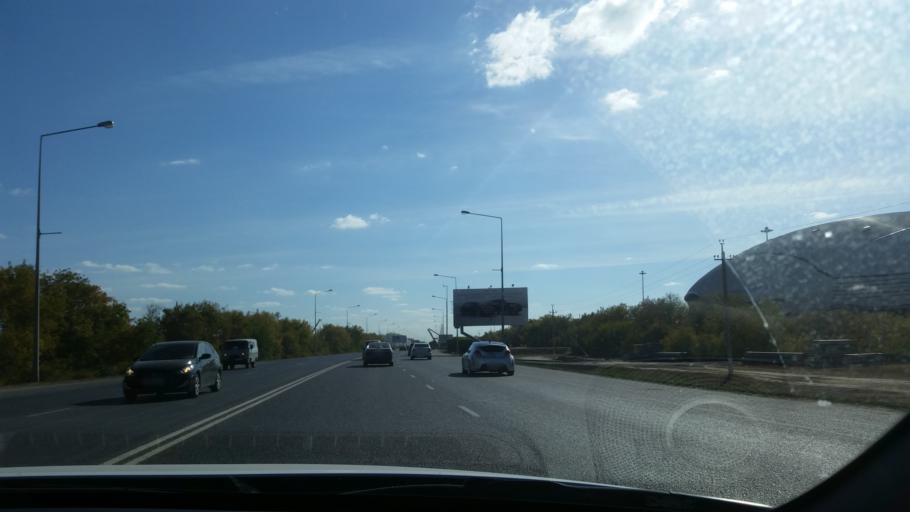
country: KZ
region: Astana Qalasy
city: Astana
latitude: 51.1124
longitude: 71.4107
